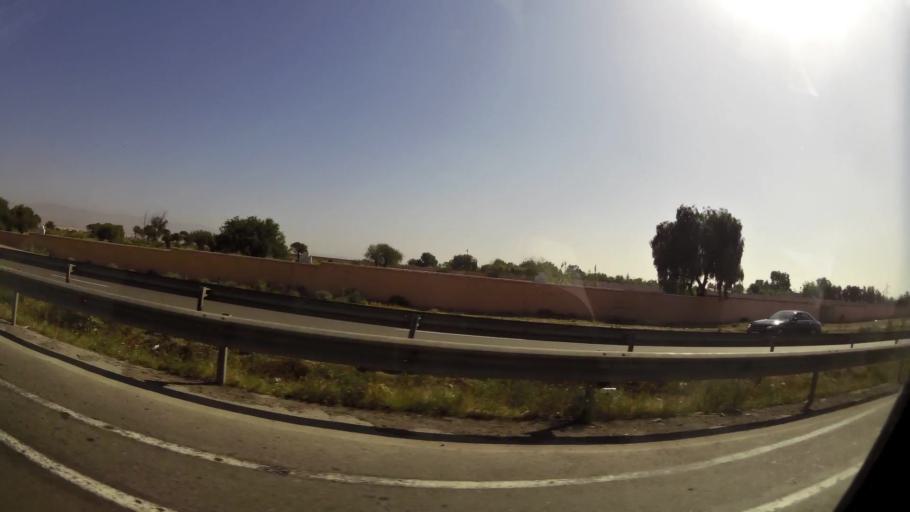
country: MA
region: Souss-Massa-Draa
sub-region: Inezgane-Ait Mellou
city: Inezgane
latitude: 30.3587
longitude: -9.4892
